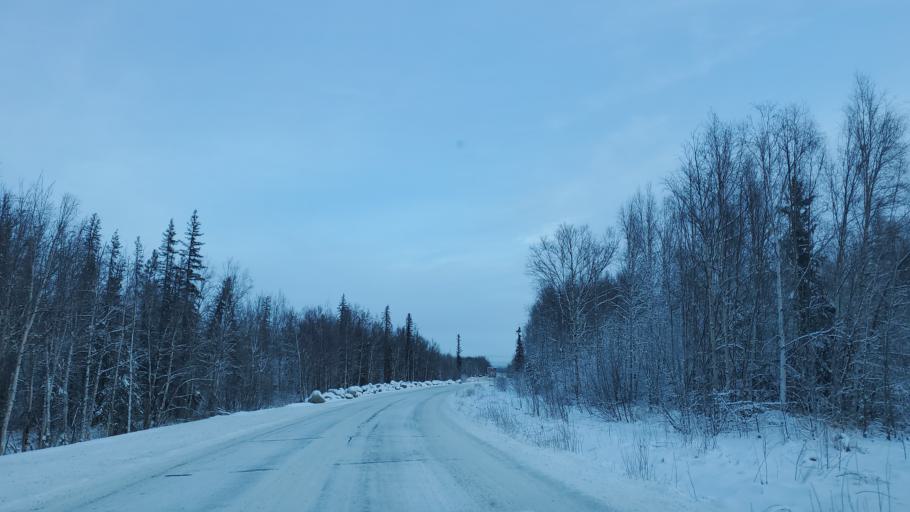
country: US
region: Alaska
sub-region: Matanuska-Susitna Borough
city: Lakes
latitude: 61.5509
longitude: -149.2989
